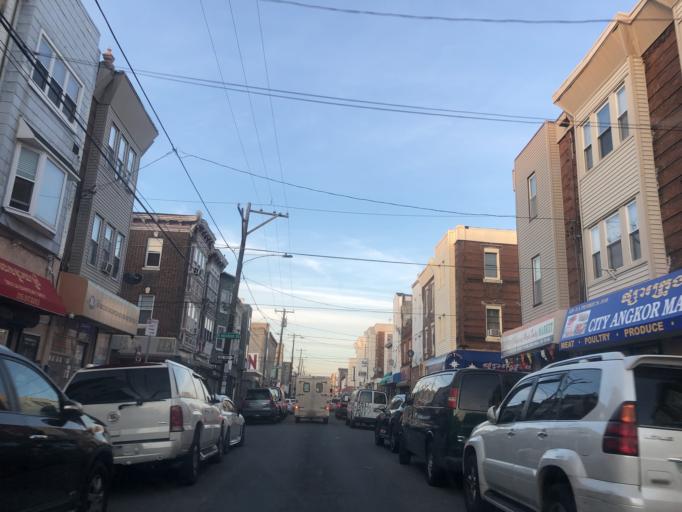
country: US
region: Pennsylvania
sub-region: Philadelphia County
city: Philadelphia
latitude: 39.9219
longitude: -75.1584
